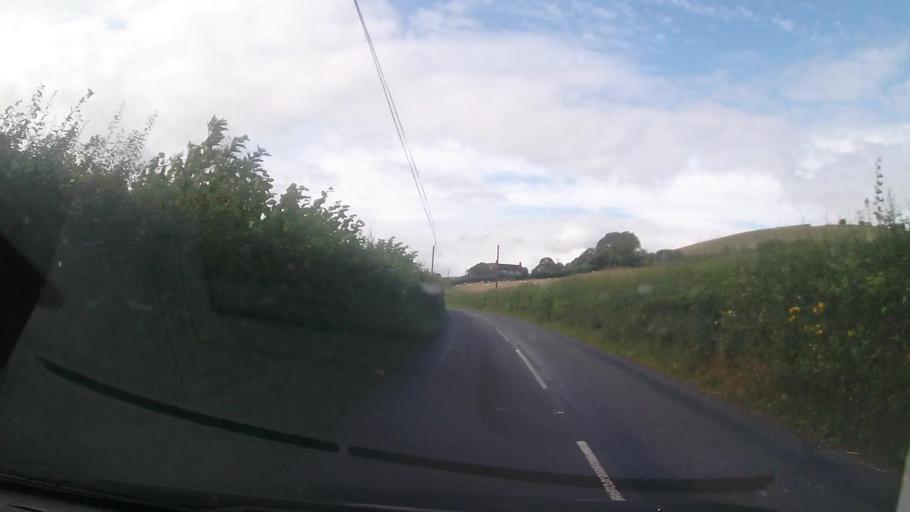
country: GB
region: England
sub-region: Shropshire
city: Acton
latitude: 52.4310
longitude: -3.0346
